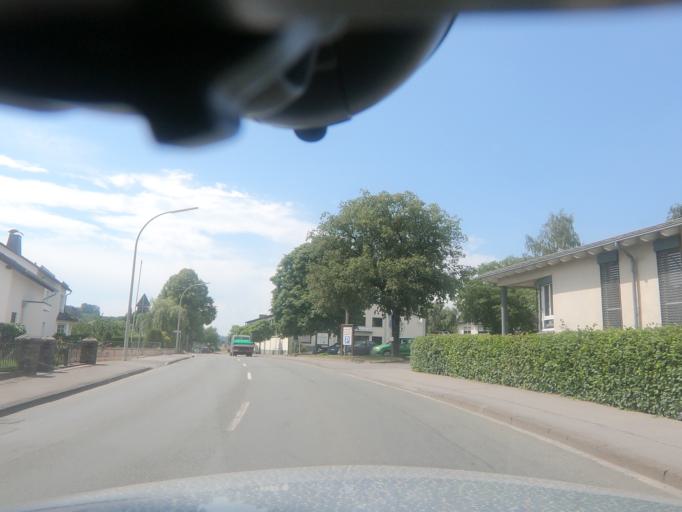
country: DE
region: North Rhine-Westphalia
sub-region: Regierungsbezirk Arnsberg
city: Sundern
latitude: 51.3245
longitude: 8.0480
